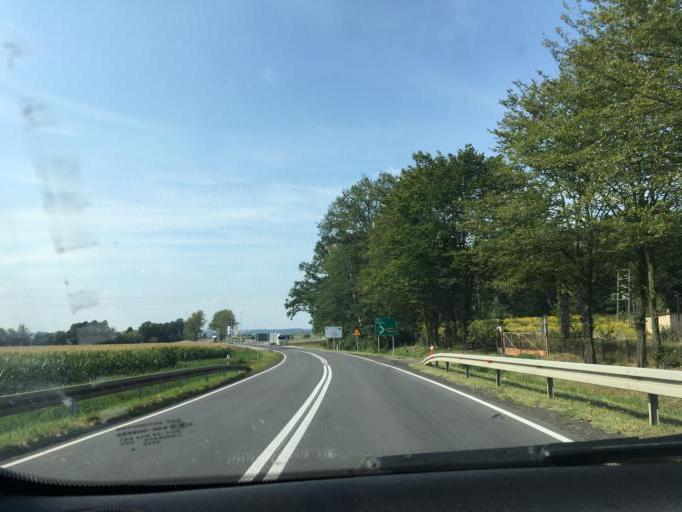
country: PL
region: Opole Voivodeship
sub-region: Powiat nyski
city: Nysa
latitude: 50.4385
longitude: 17.4069
